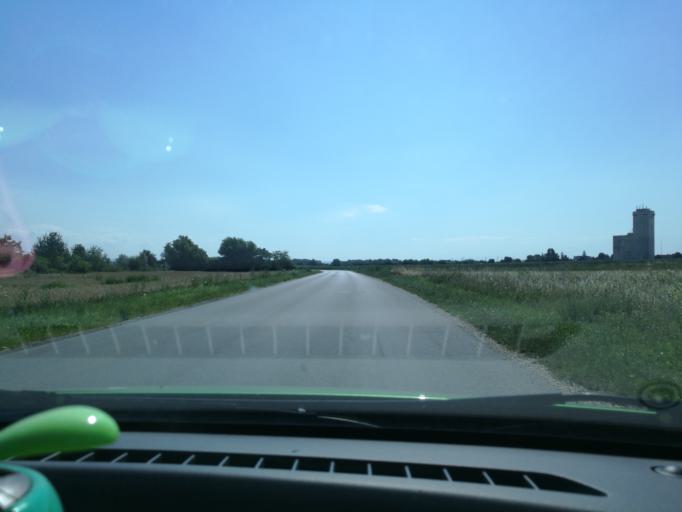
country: AT
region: Lower Austria
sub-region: Politischer Bezirk Ganserndorf
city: Ganserndorf
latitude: 48.3462
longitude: 16.7298
